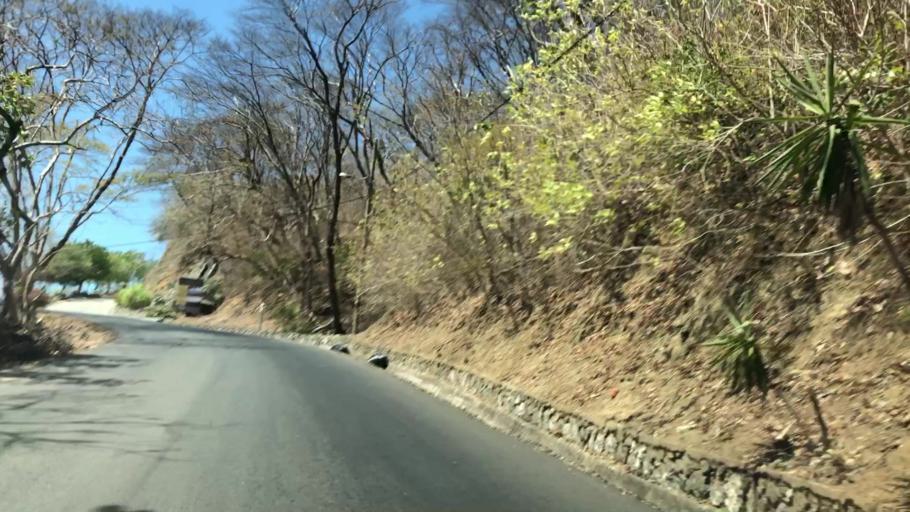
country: CR
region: Guanacaste
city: Belen
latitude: 10.3492
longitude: -85.8218
